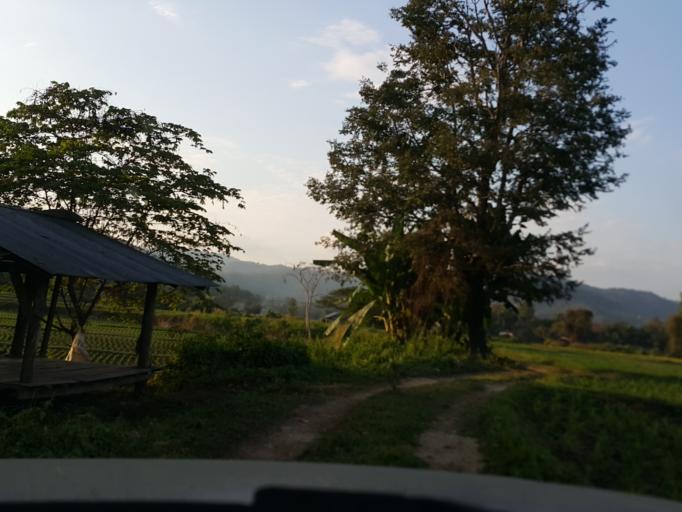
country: TH
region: Lamphun
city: Ban Thi
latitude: 18.5916
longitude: 99.2789
